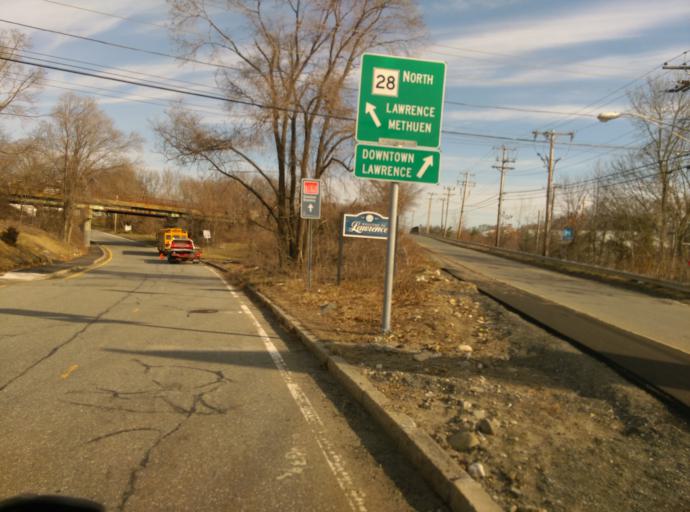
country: US
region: Massachusetts
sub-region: Essex County
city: North Andover
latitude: 42.6826
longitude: -71.1525
